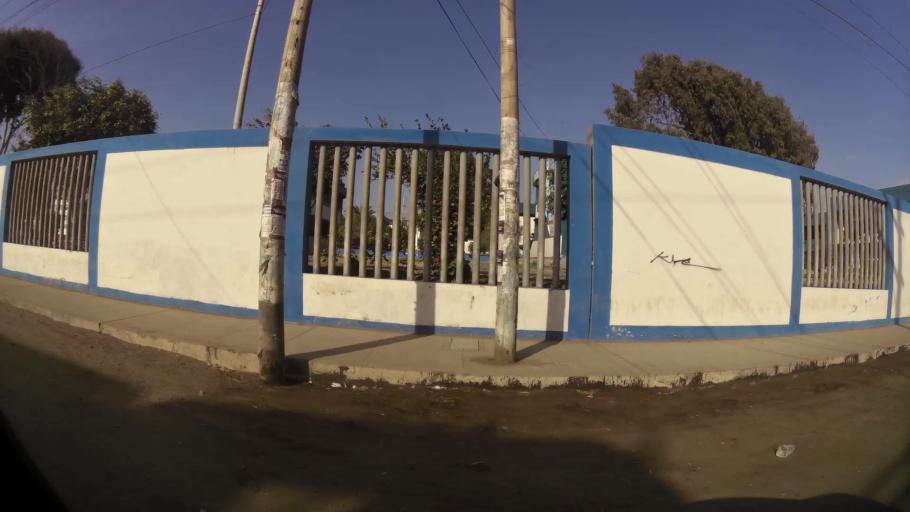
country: PE
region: Lima
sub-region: Huaura
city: Huacho
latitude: -11.1240
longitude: -77.6104
